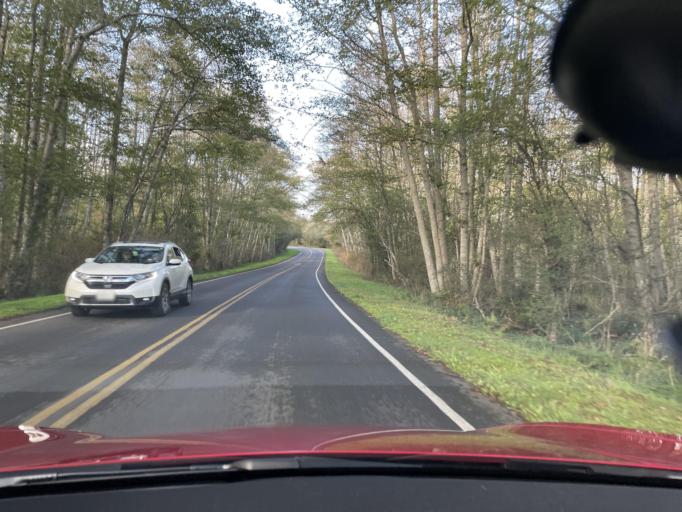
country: US
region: Washington
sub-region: San Juan County
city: Friday Harbor
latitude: 48.4663
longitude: -123.0063
